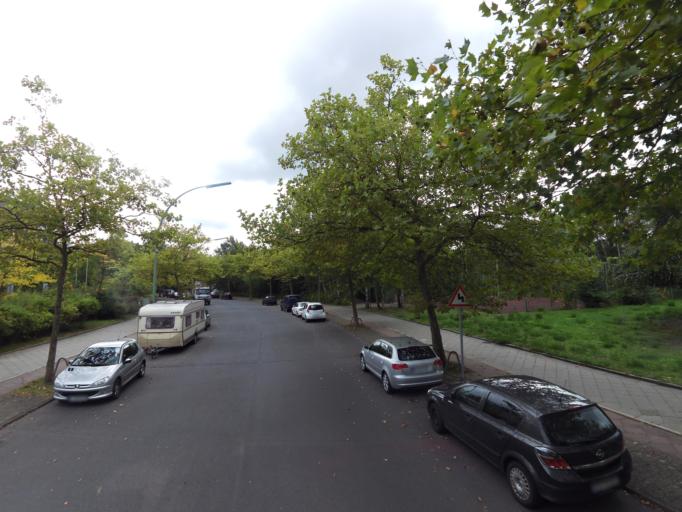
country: DE
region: Berlin
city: Lichterfelde
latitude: 52.4118
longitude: 13.3036
